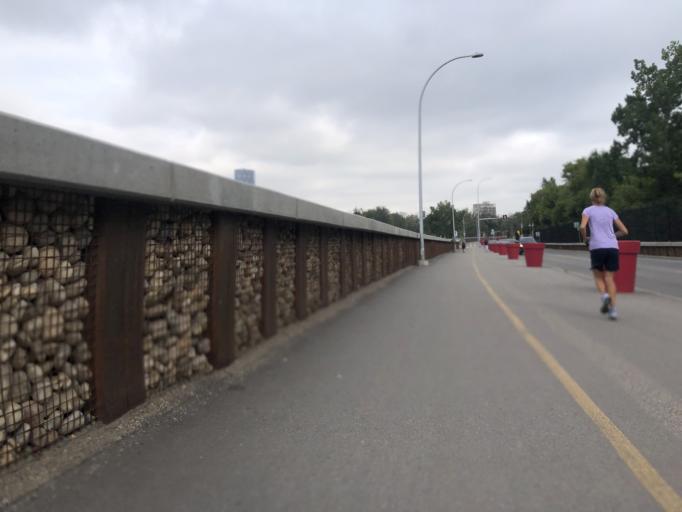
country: CA
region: Alberta
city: Calgary
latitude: 51.0452
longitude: -114.0338
